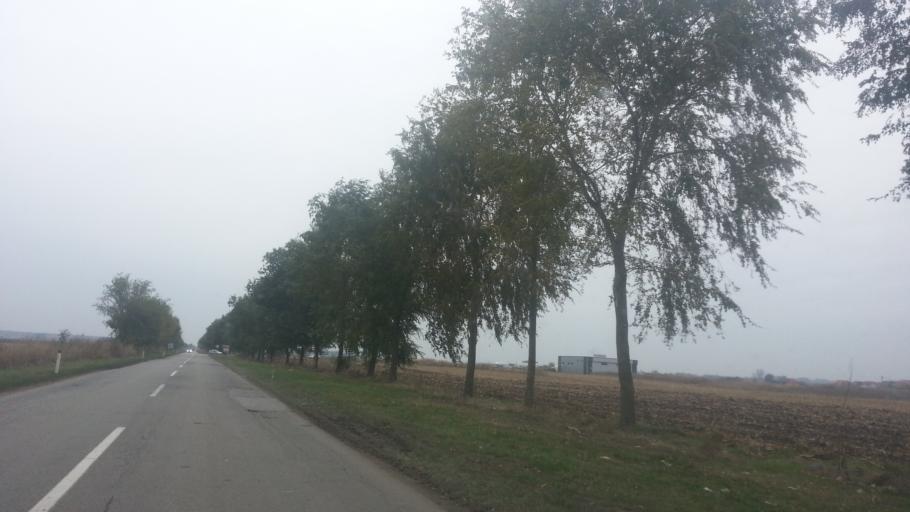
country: RS
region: Autonomna Pokrajina Vojvodina
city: Nova Pazova
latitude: 44.9593
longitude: 20.2093
